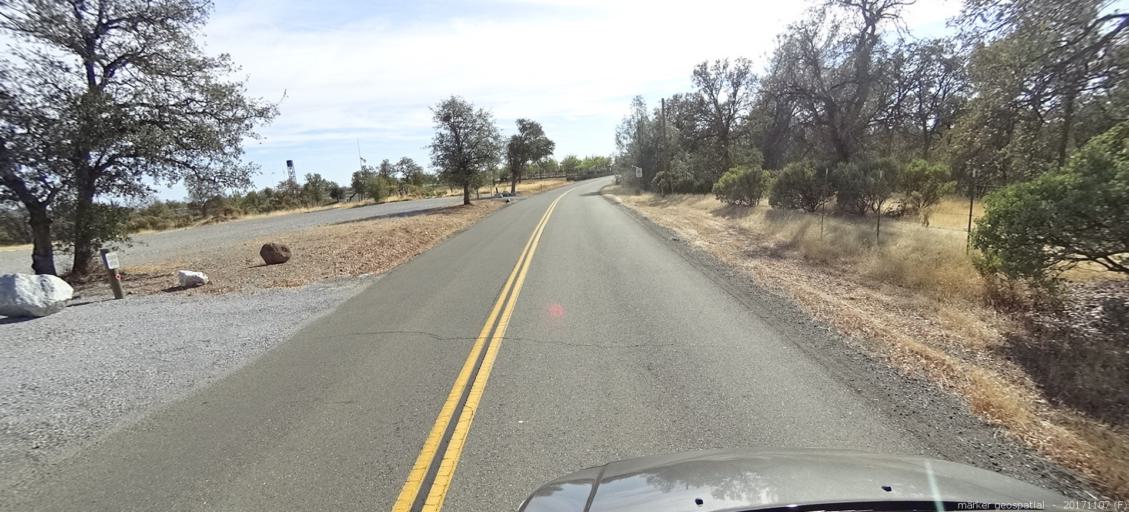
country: US
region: California
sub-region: Shasta County
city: Shasta
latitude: 40.4797
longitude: -122.5453
